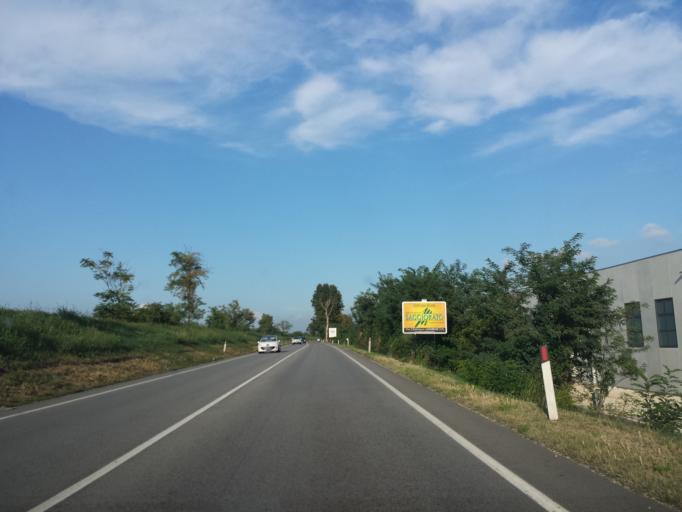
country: IT
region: Veneto
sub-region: Provincia di Vicenza
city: Montebello Vicentino
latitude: 45.4478
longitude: 11.3802
